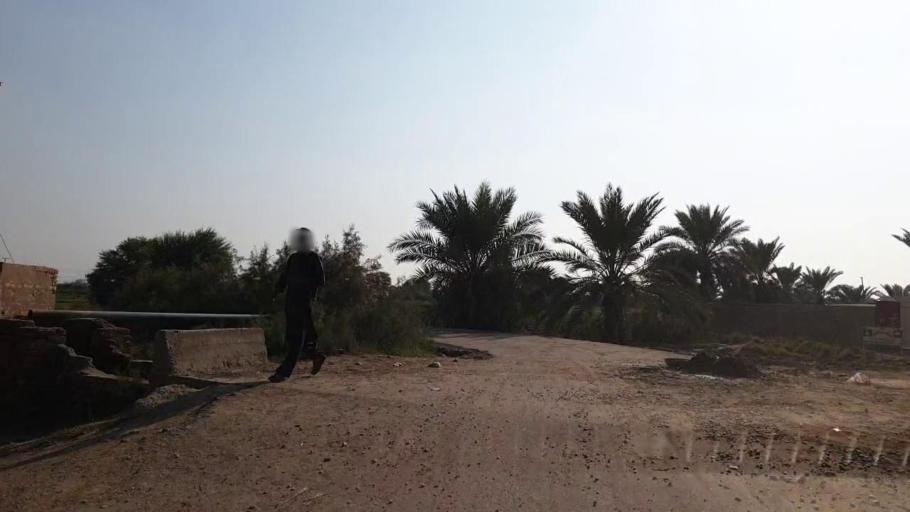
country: PK
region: Sindh
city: Sehwan
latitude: 26.4484
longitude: 67.8143
